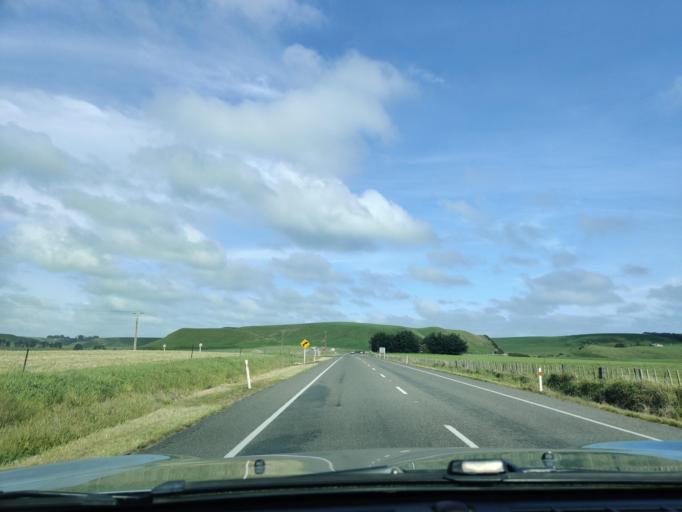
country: NZ
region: Manawatu-Wanganui
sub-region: Wanganui District
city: Wanganui
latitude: -40.0093
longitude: 175.1693
